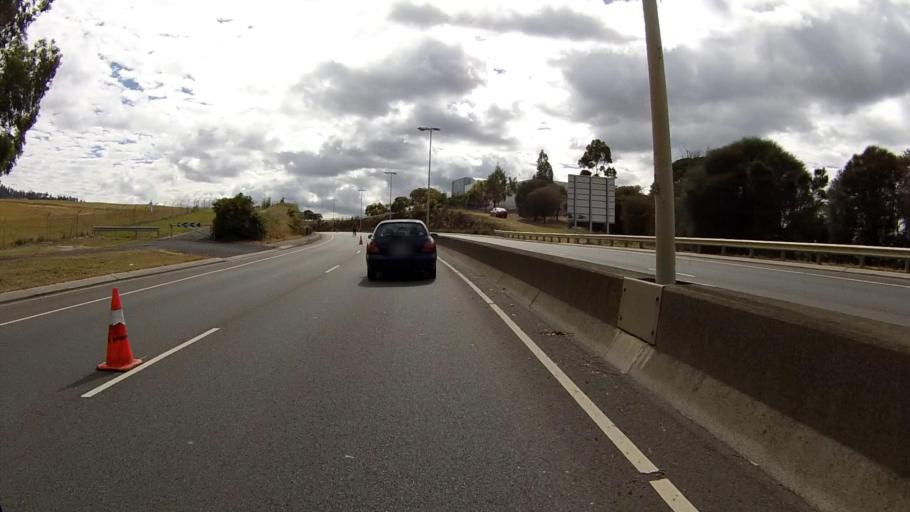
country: AU
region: Tasmania
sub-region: Glenorchy
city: Goodwood
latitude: -42.8234
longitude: 147.2990
